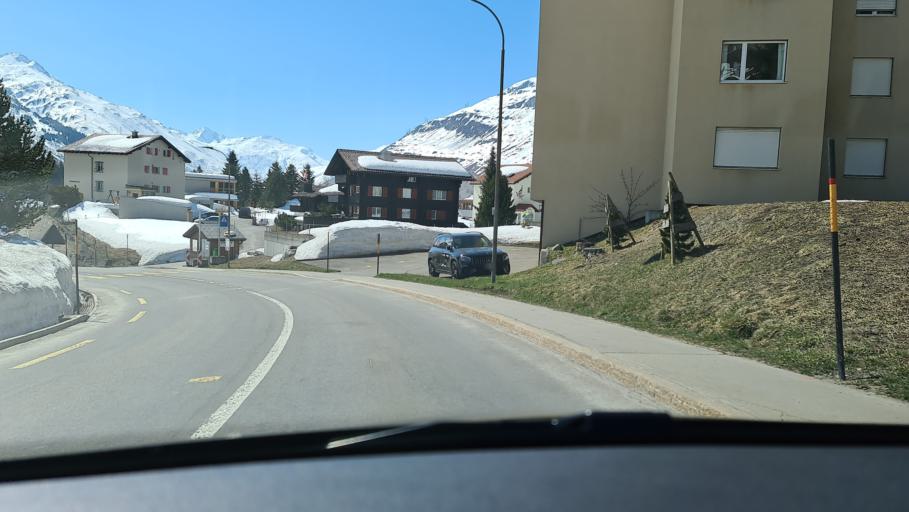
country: CH
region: Uri
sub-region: Uri
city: Andermatt
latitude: 46.6356
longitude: 8.6001
